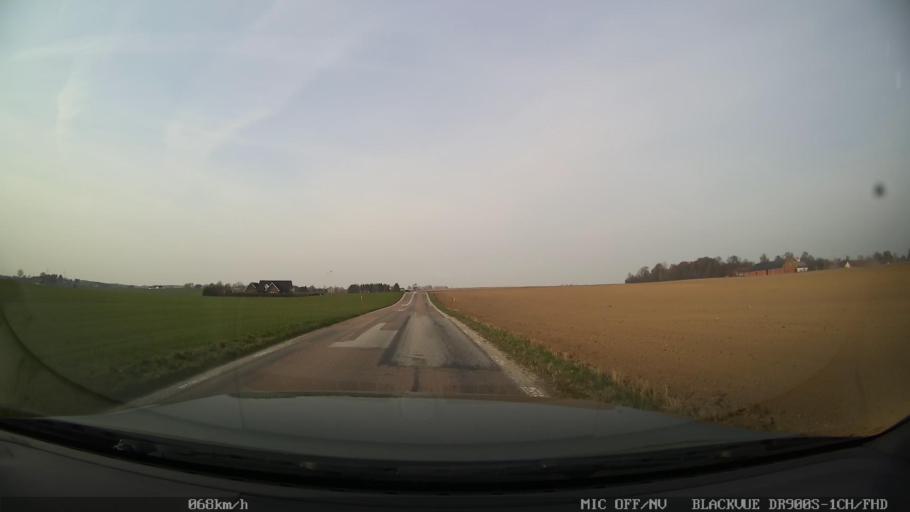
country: SE
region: Skane
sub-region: Ystads Kommun
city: Ystad
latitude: 55.4494
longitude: 13.8316
